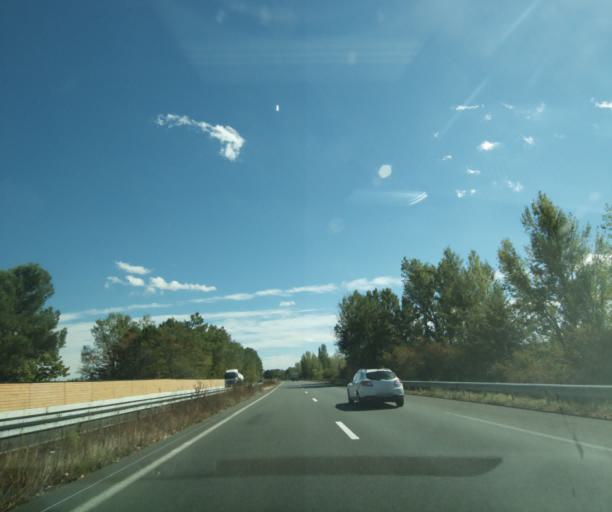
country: FR
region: Aquitaine
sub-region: Departement du Lot-et-Garonne
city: Buzet-sur-Baise
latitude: 44.2577
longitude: 0.2888
